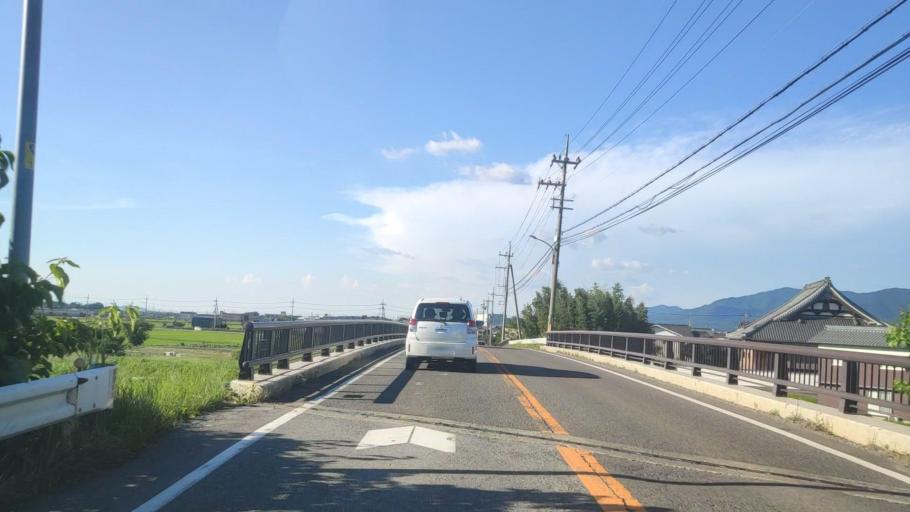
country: JP
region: Shiga Prefecture
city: Youkaichi
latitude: 35.0762
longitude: 136.2486
